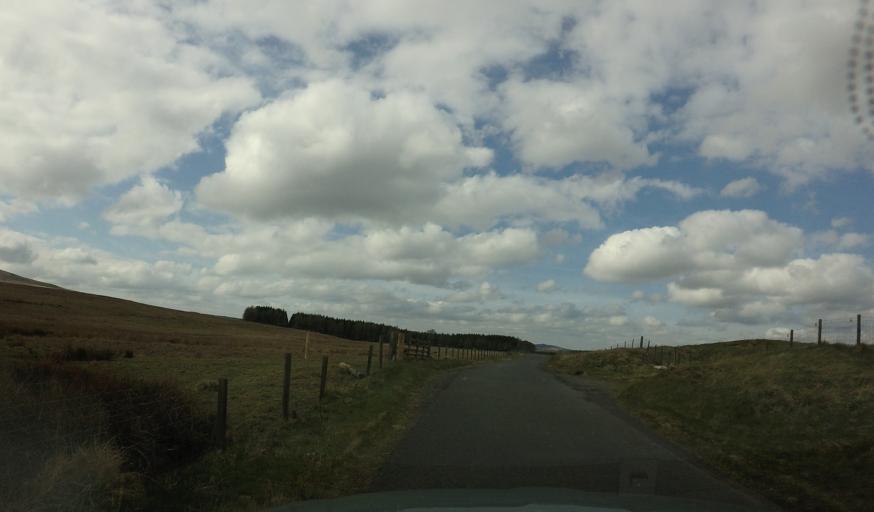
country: GB
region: Scotland
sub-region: Midlothian
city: Penicuik
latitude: 55.7605
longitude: -3.1621
